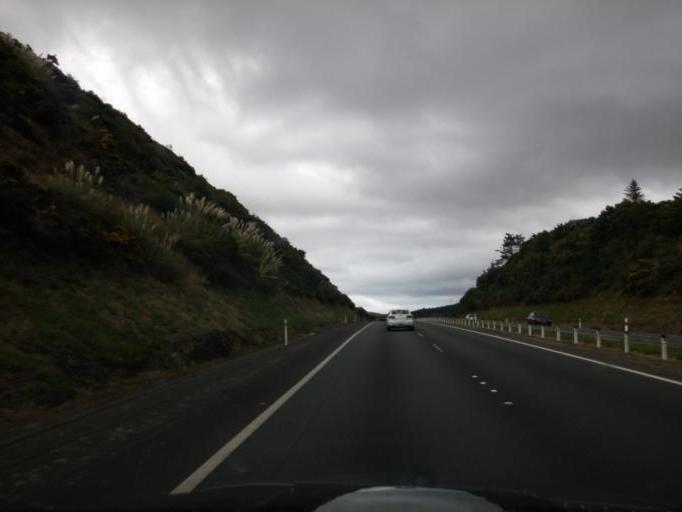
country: NZ
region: Wellington
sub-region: Porirua City
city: Porirua
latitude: -41.1708
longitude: 174.8315
